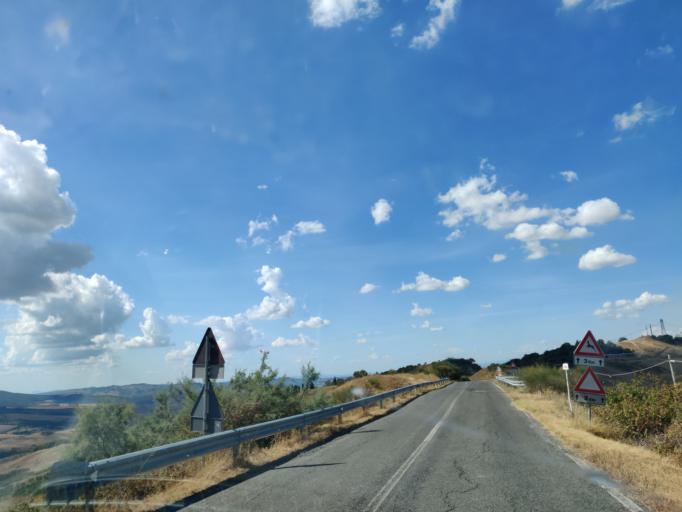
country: IT
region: Tuscany
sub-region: Provincia di Siena
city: Radicofani
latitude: 42.9512
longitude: 11.7303
